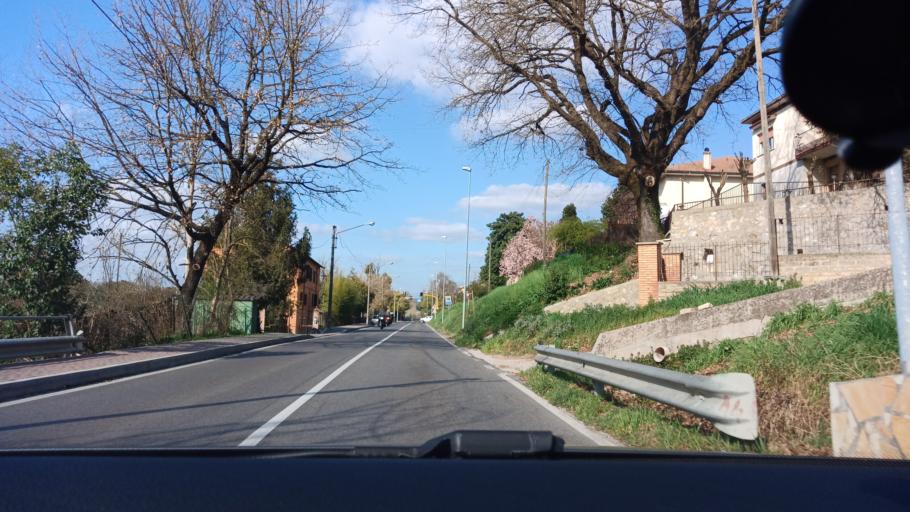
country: IT
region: Latium
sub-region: Citta metropolitana di Roma Capitale
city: Torrita Tiberina
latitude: 42.2444
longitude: 12.6339
